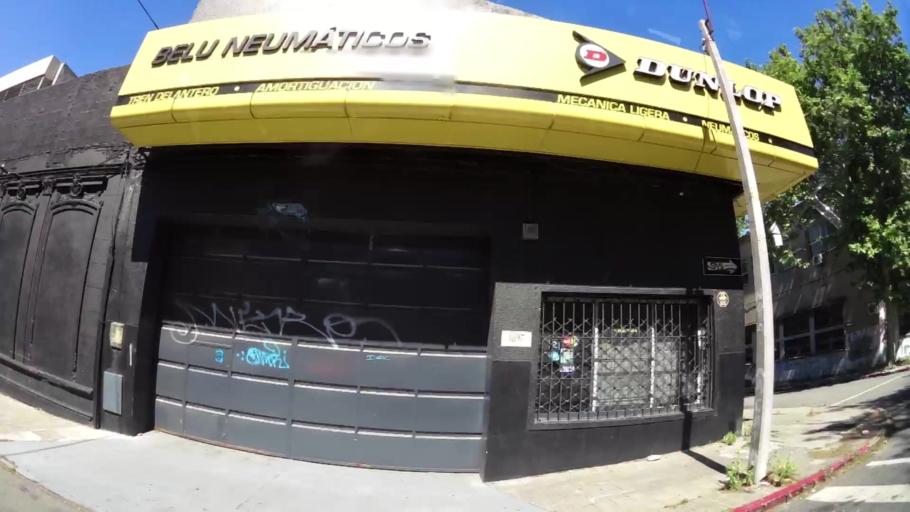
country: UY
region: Montevideo
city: Montevideo
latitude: -34.8964
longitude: -56.1848
